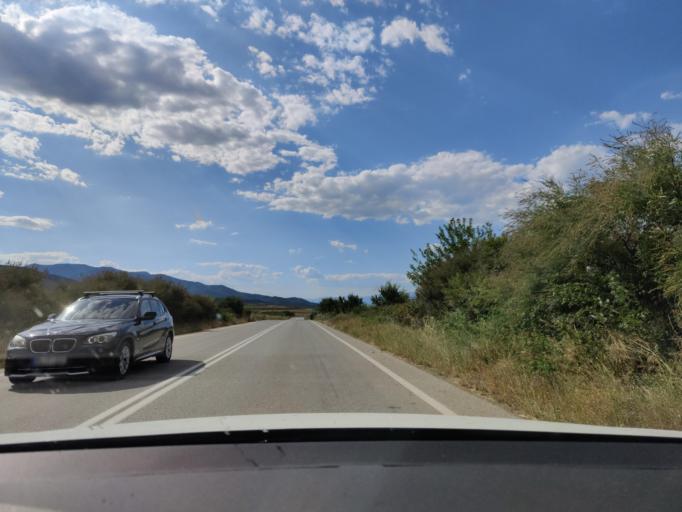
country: GR
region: Central Macedonia
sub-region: Nomos Serron
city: Strymoniko
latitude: 41.0936
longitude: 23.2745
